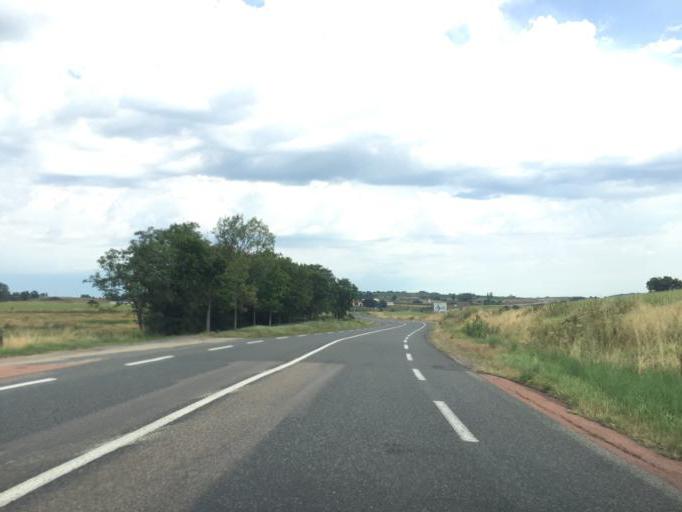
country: FR
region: Rhone-Alpes
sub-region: Departement du Rhone
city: Saint-Romain-de-Popey
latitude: 45.8775
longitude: 4.5303
